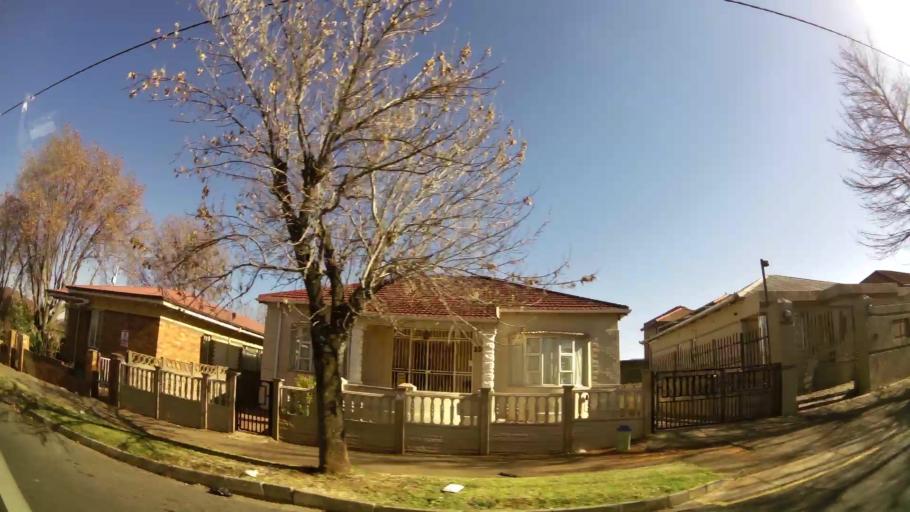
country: ZA
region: Gauteng
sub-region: City of Johannesburg Metropolitan Municipality
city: Johannesburg
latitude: -26.1956
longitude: 27.9969
